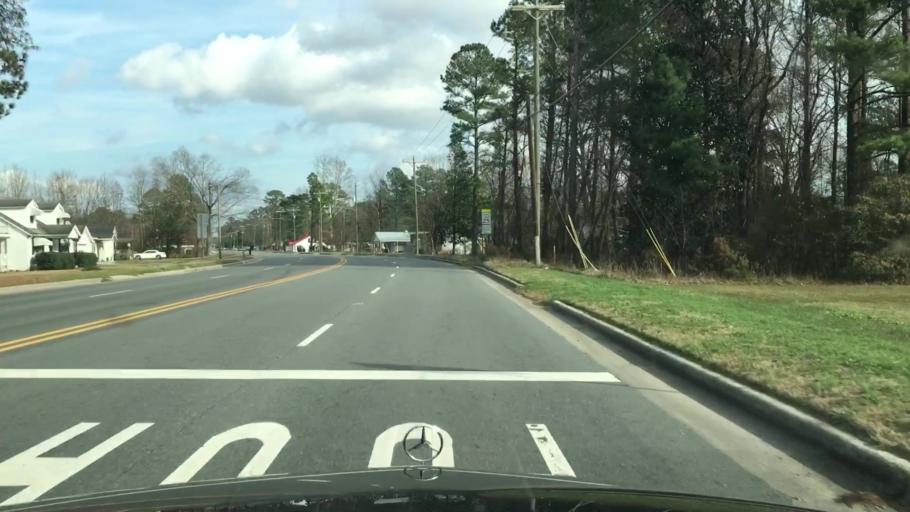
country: US
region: North Carolina
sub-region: Duplin County
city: Warsaw
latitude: 34.9943
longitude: -78.1118
